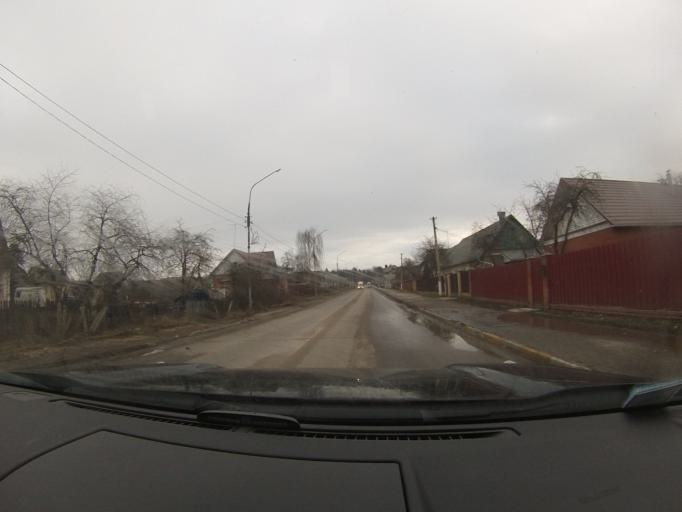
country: RU
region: Moskovskaya
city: Peski
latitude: 55.2535
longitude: 38.7649
